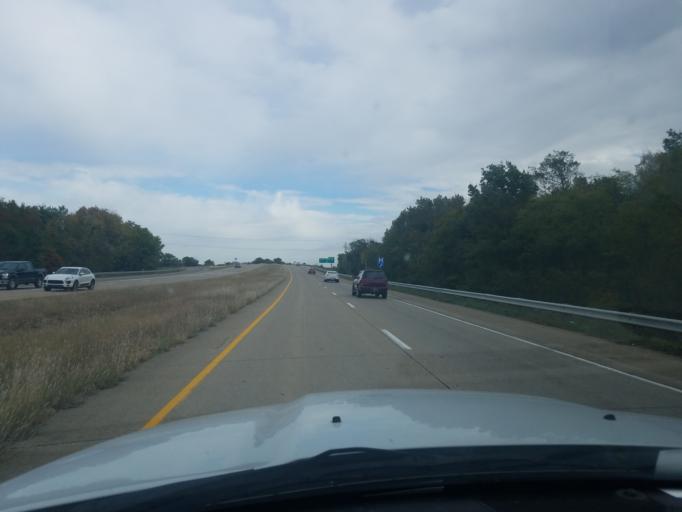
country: US
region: Indiana
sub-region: Vanderburgh County
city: Evansville
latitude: 37.9388
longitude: -87.4985
